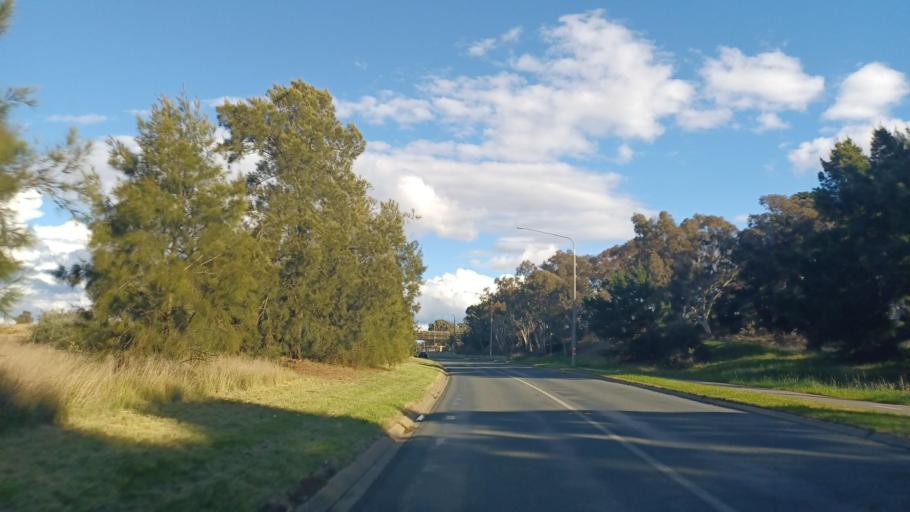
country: AU
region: Australian Capital Territory
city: Belconnen
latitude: -35.1867
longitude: 149.0725
